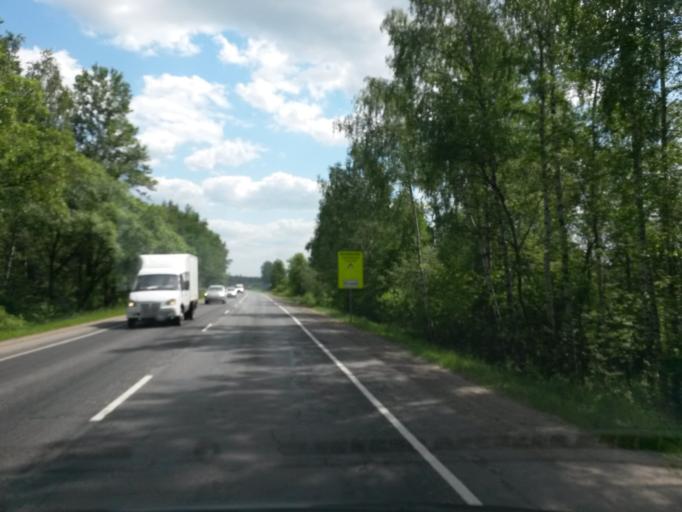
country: RU
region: Jaroslavl
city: Yaroslavl
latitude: 57.5528
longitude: 39.8820
